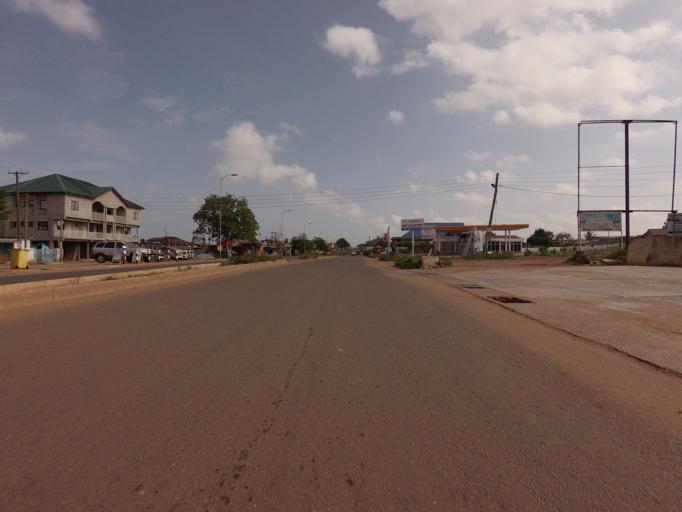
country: GH
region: Greater Accra
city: Tema
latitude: 5.6689
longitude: -0.0473
